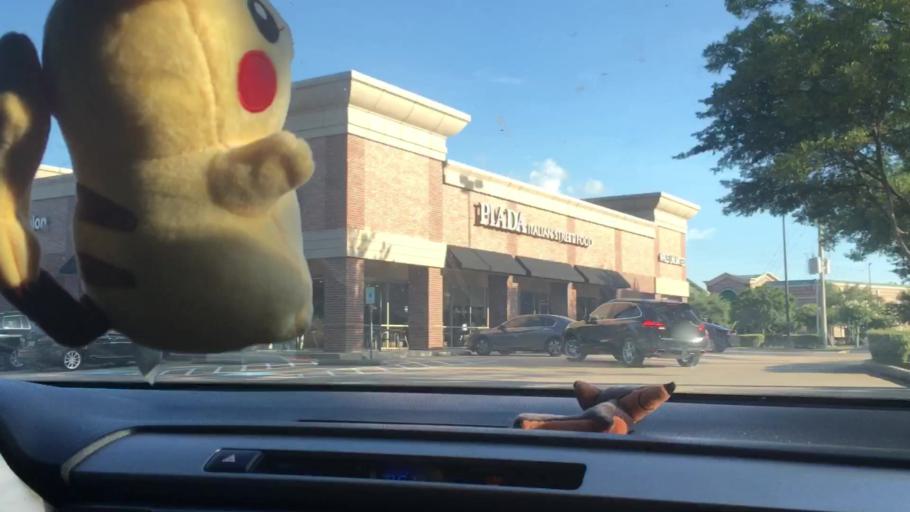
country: US
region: Texas
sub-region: Fort Bend County
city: Sugar Land
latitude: 29.5990
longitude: -95.6246
